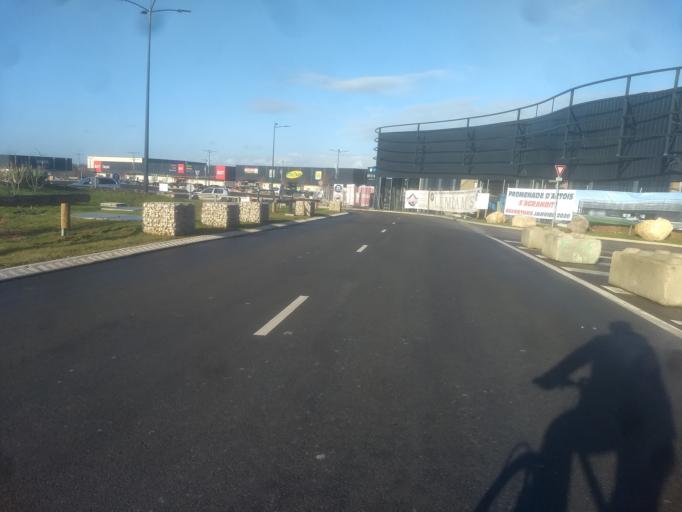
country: FR
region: Nord-Pas-de-Calais
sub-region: Departement du Pas-de-Calais
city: Anzin-Saint-Aubin
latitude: 50.3053
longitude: 2.7281
